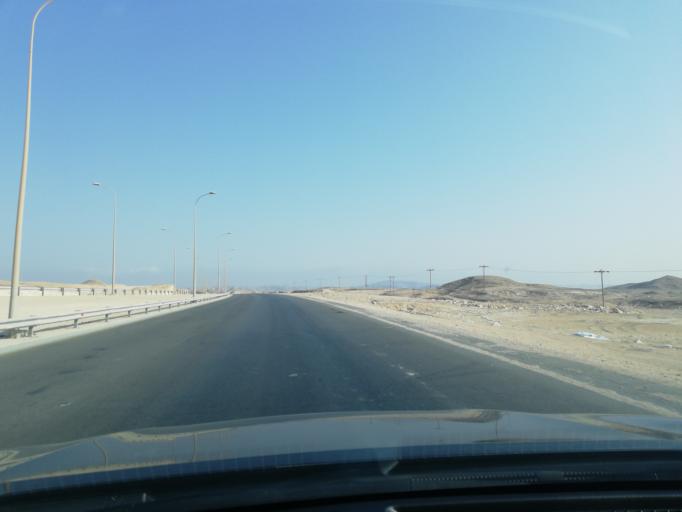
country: OM
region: Zufar
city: Salalah
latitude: 17.3523
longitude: 54.0762
